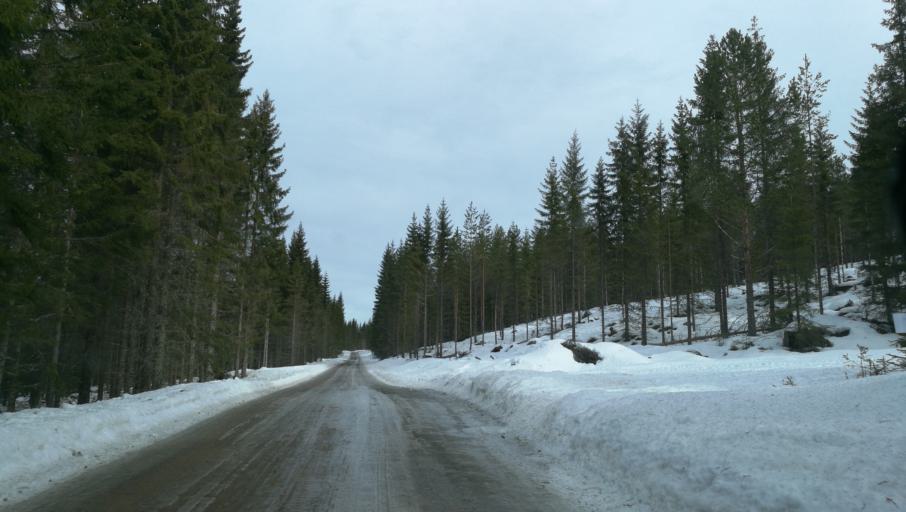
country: SE
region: Vaermland
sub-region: Torsby Kommun
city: Torsby
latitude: 60.6512
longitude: 12.8015
